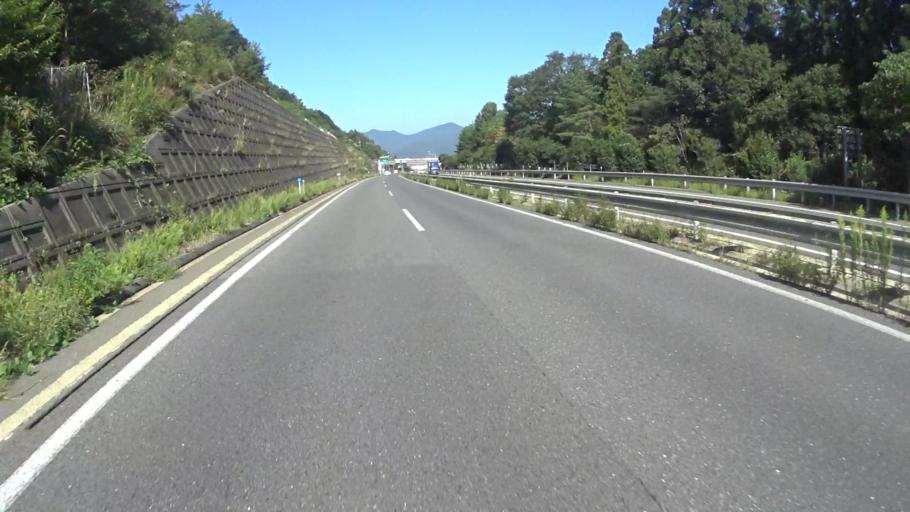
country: JP
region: Kyoto
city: Kameoka
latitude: 35.0034
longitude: 135.5677
